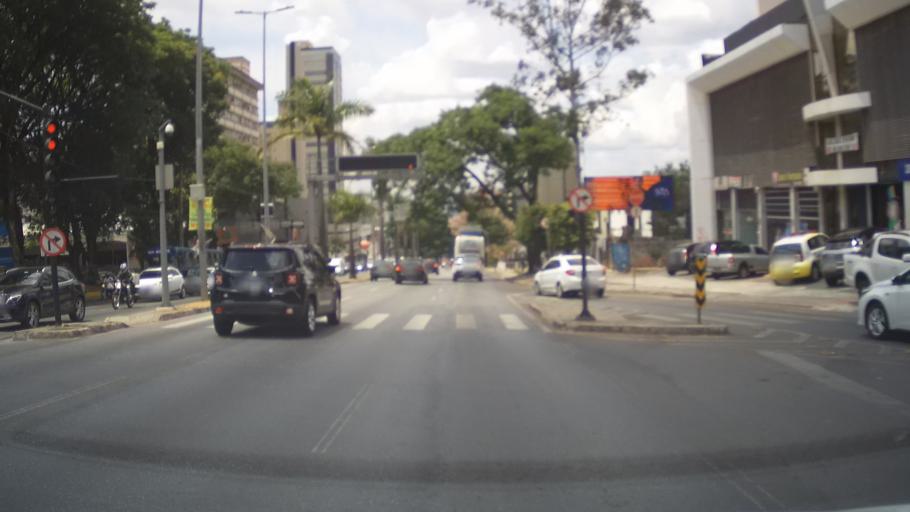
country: BR
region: Minas Gerais
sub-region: Belo Horizonte
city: Belo Horizonte
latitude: -19.9521
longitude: -43.9380
